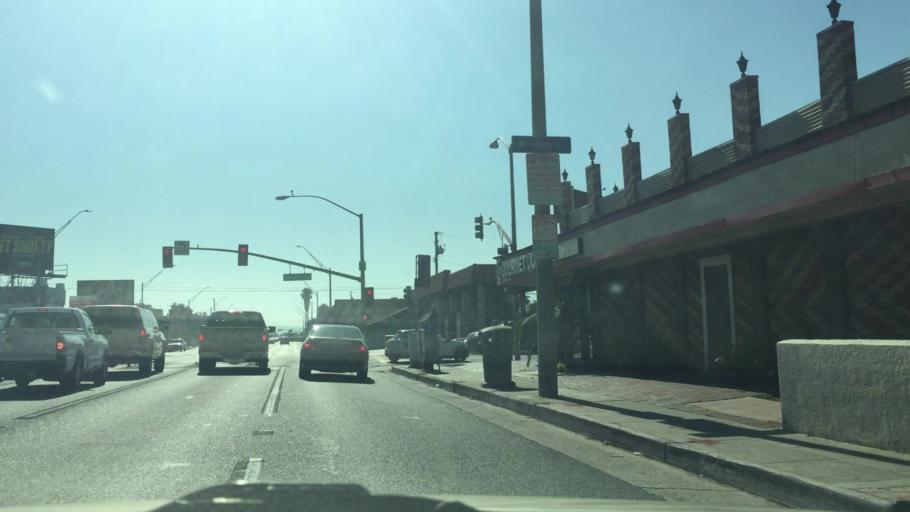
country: US
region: California
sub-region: Los Angeles County
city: Signal Hill
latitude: 33.7900
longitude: -118.1845
